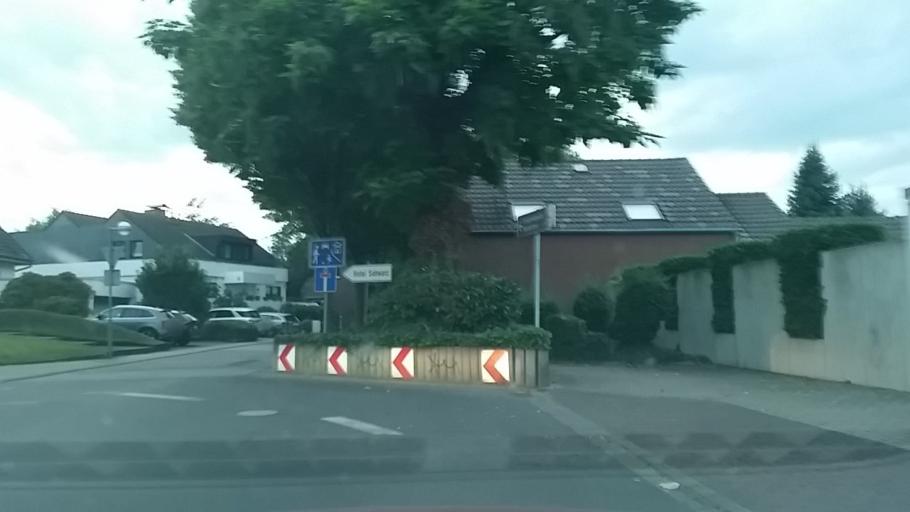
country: DE
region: North Rhine-Westphalia
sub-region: Regierungsbezirk Dusseldorf
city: Meerbusch
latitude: 51.2421
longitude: 6.6877
